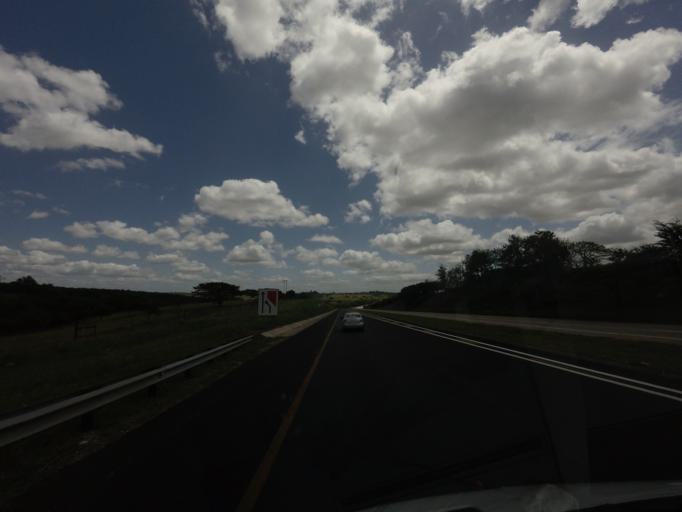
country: ZA
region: KwaZulu-Natal
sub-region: uThungulu District Municipality
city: KwaMbonambi
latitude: -28.5097
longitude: 32.1375
